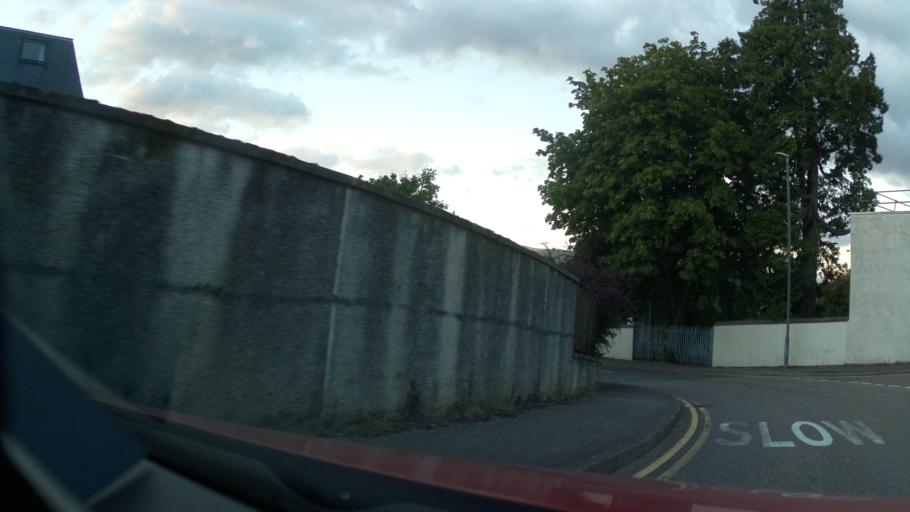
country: GB
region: Scotland
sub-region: Highland
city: Fort William
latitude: 56.8189
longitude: -5.1061
